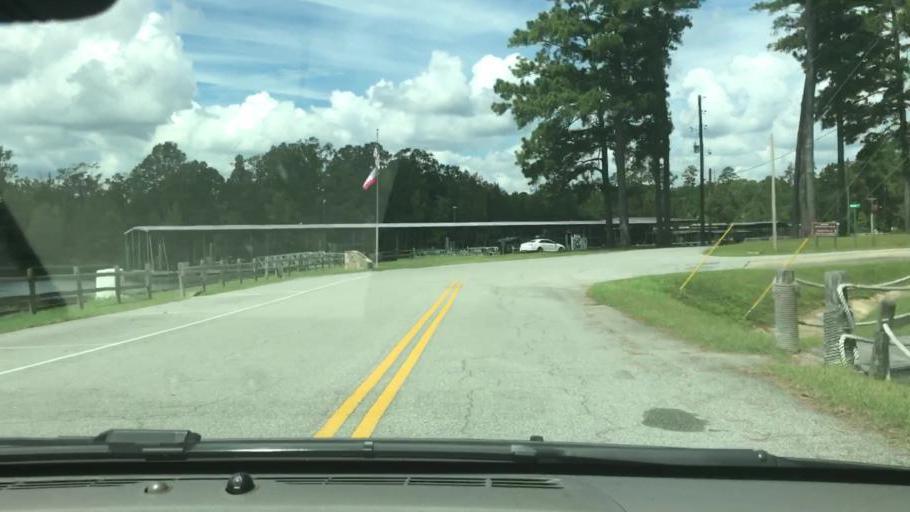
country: US
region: Georgia
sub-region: Quitman County
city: Georgetown
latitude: 32.0896
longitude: -85.0434
